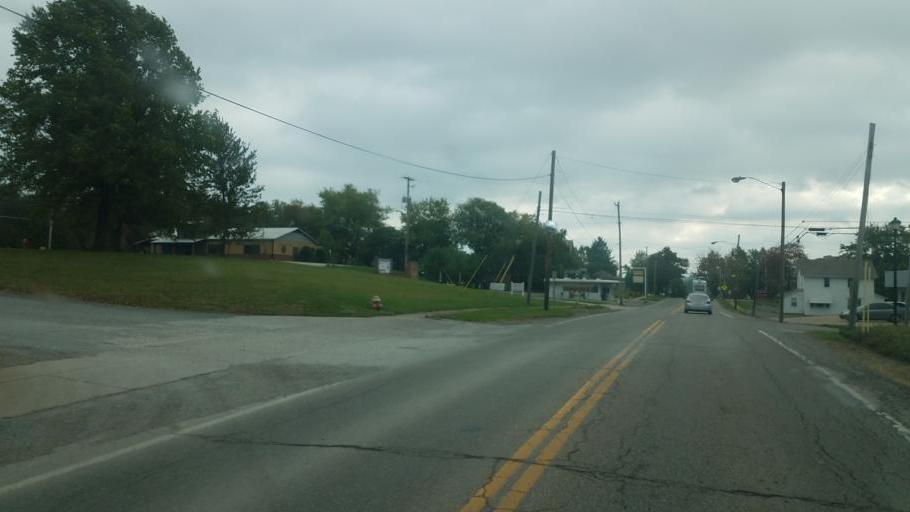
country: US
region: Ohio
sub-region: Tuscarawas County
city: Sugarcreek
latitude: 40.5081
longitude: -81.6430
